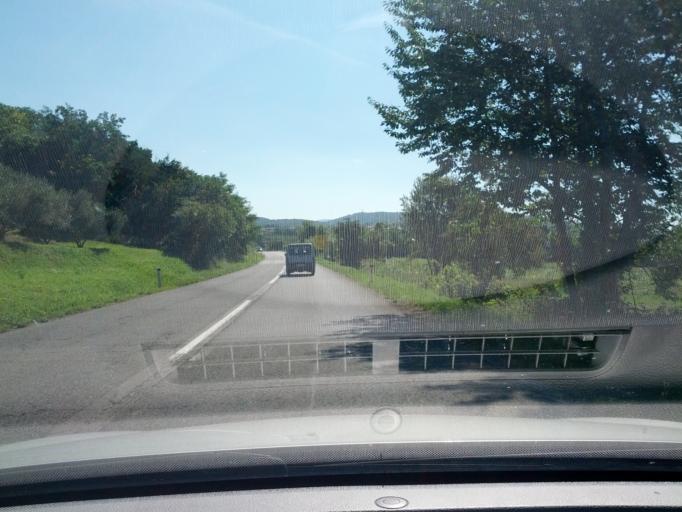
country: SI
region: Koper-Capodistria
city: Hrvatini
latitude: 45.5685
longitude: 13.7674
